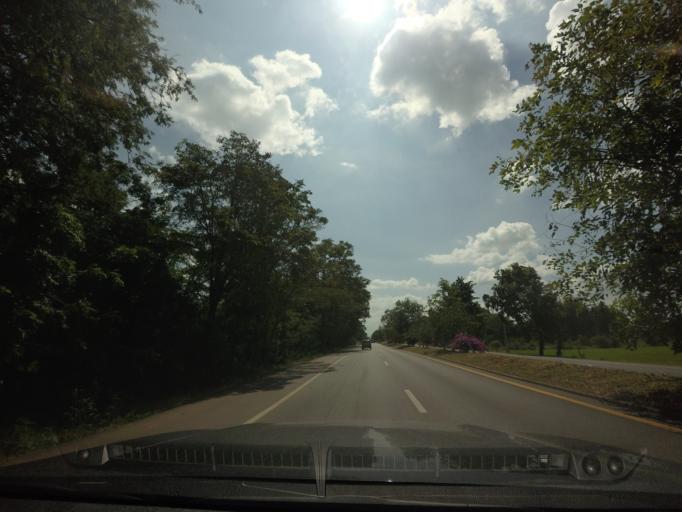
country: TH
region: Phetchabun
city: Nong Phai
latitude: 15.9482
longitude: 101.0357
